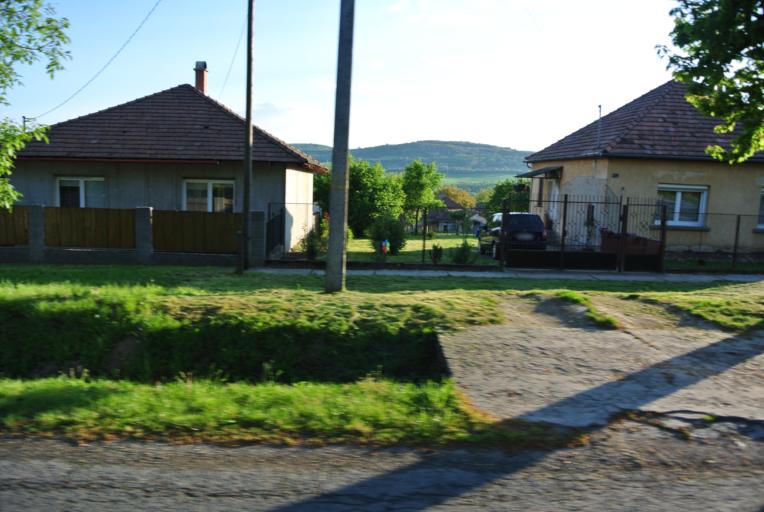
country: HU
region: Komarom-Esztergom
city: Sarisap
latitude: 47.6676
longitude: 18.6912
